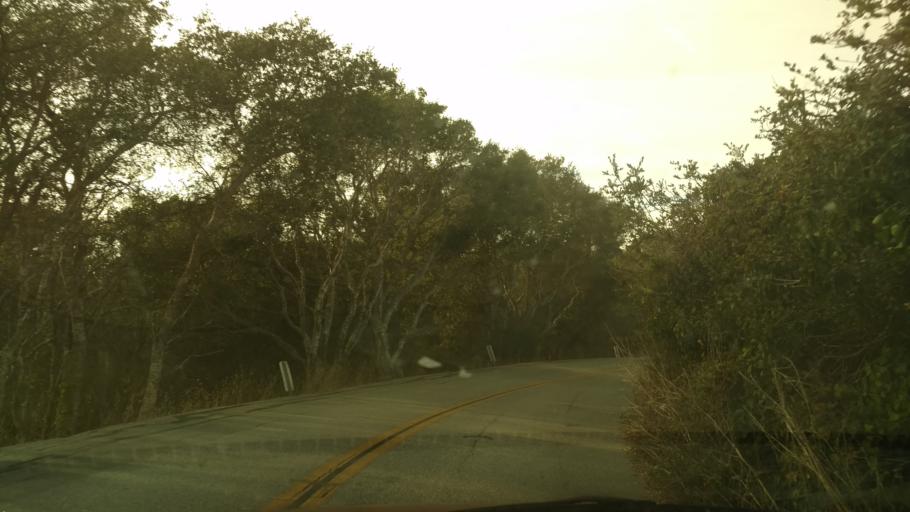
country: US
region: California
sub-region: Santa Cruz County
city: Rio Del Mar
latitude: 36.9664
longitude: -121.8767
